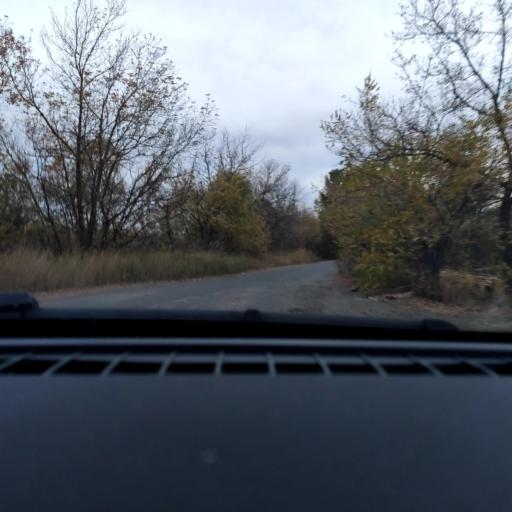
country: RU
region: Voronezj
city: Maslovka
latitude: 51.6208
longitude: 39.2614
